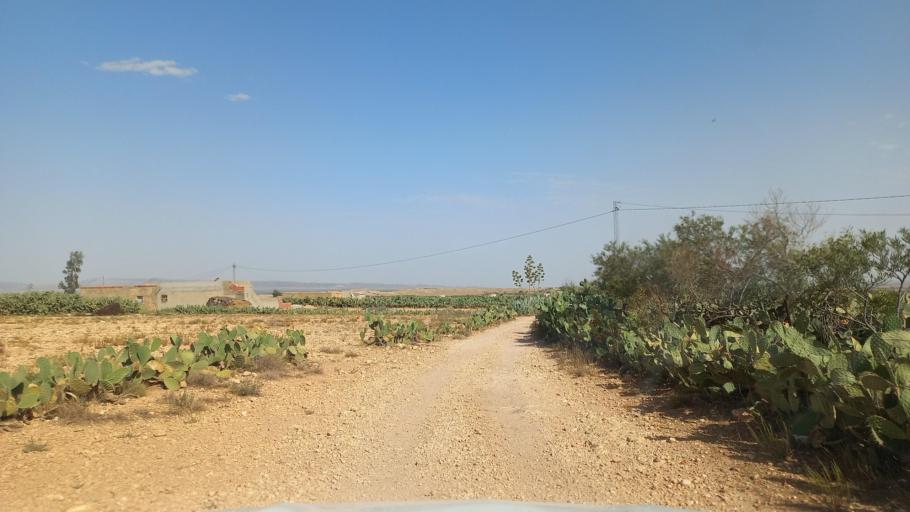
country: TN
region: Al Qasrayn
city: Kasserine
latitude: 35.2832
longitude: 8.9469
